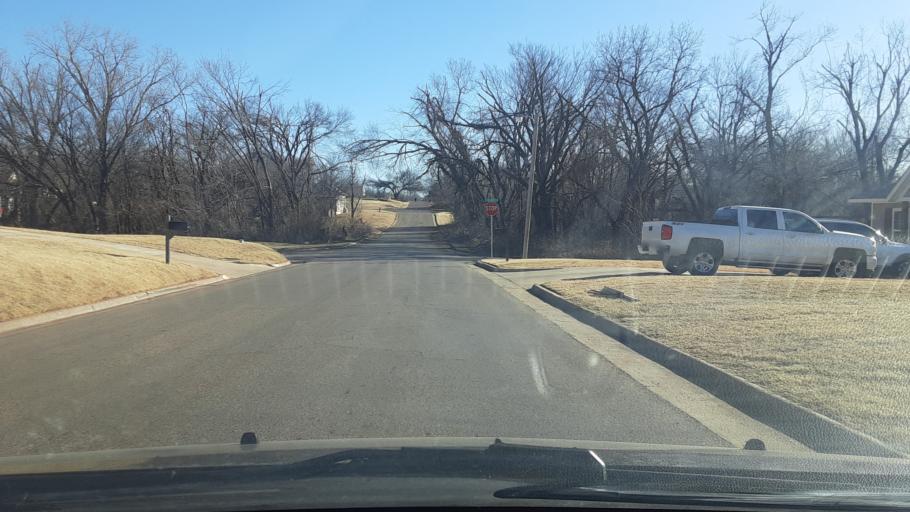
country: US
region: Oklahoma
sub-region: Logan County
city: Guthrie
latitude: 35.8728
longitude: -97.4168
